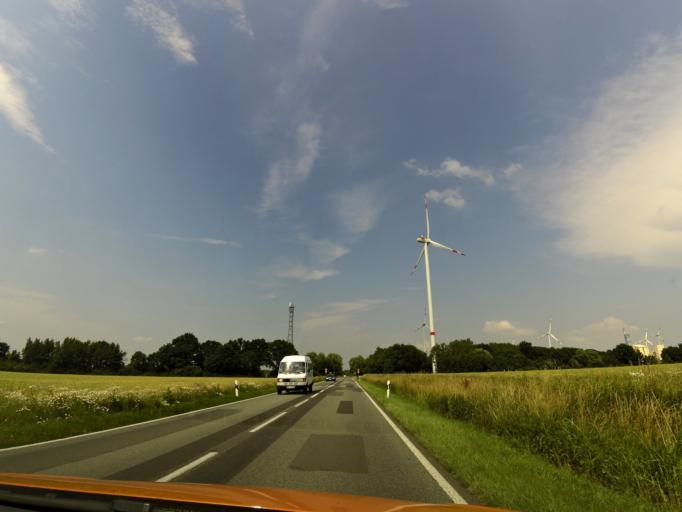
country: DE
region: Brandenburg
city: Gerdshagen
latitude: 53.2264
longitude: 12.2050
